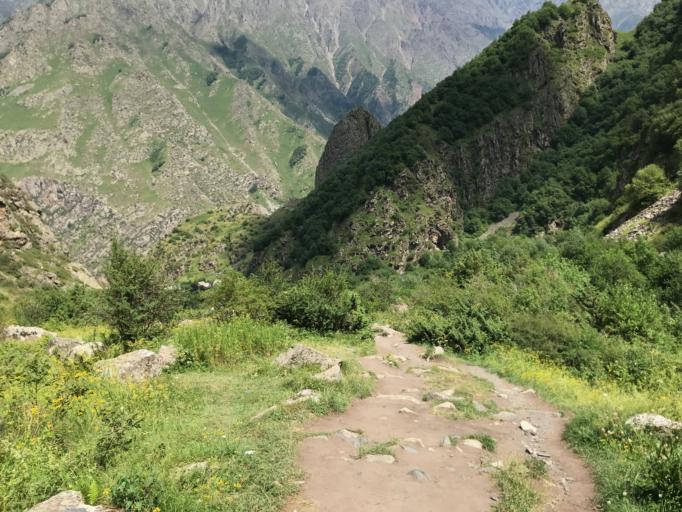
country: GE
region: Mtskheta-Mtianeti
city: Step'antsminda
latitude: 42.7049
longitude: 44.6181
